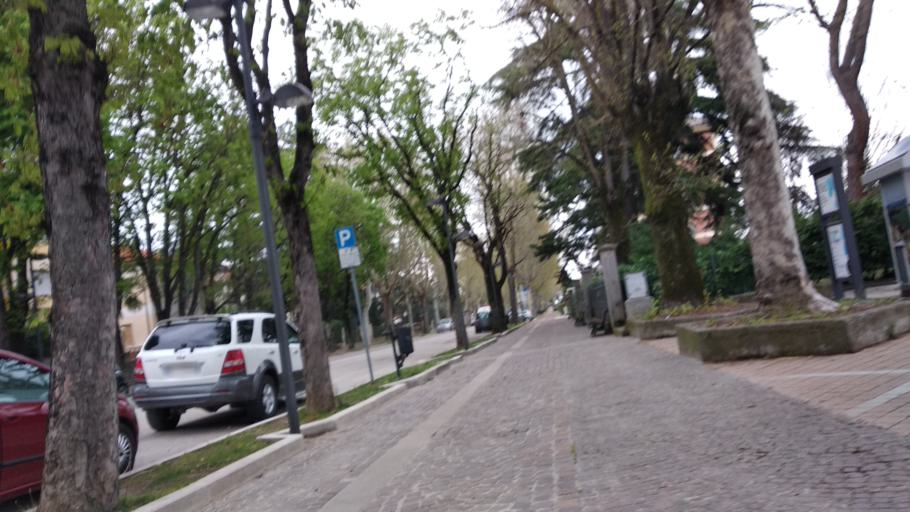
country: IT
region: Emilia-Romagna
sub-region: Forli-Cesena
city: Castrocaro Terme
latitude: 44.1740
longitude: 11.9496
